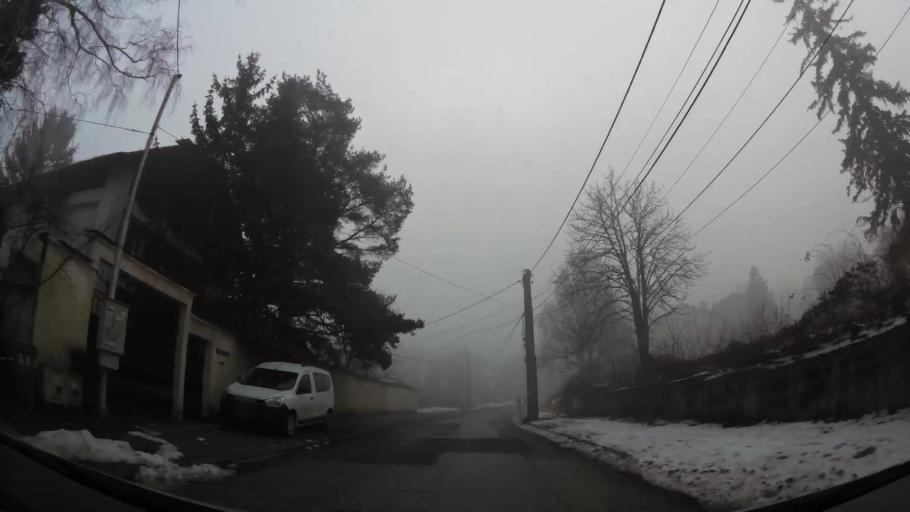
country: BG
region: Sofia-Capital
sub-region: Stolichna Obshtina
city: Sofia
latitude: 42.6584
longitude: 23.2523
